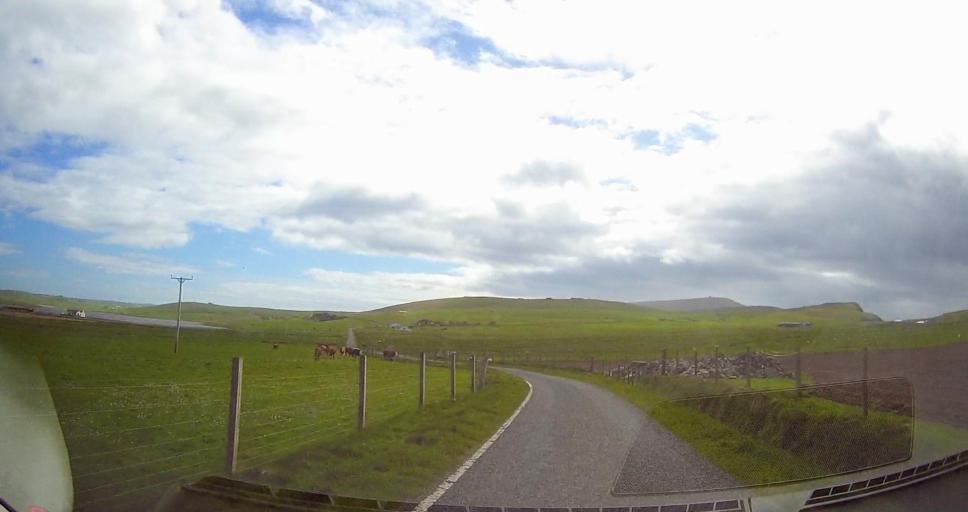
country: GB
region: Scotland
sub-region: Shetland Islands
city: Sandwick
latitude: 59.9387
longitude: -1.3463
